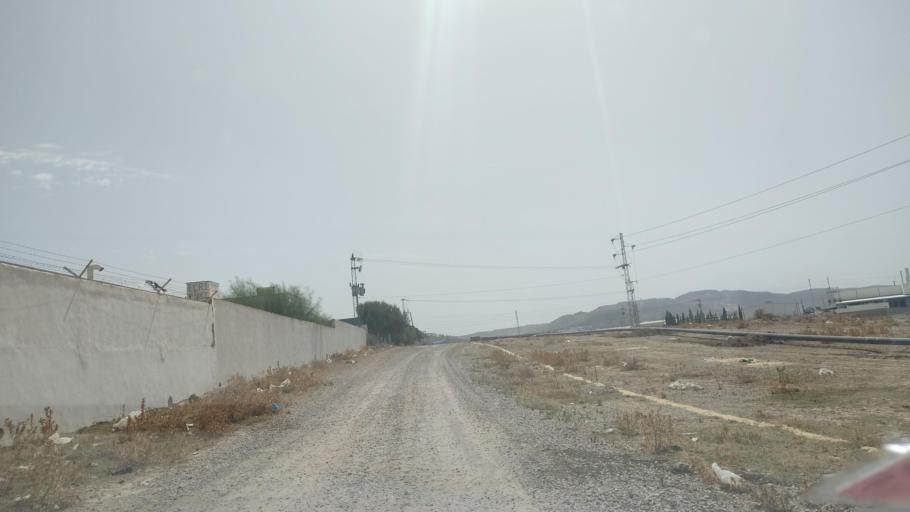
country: TN
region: Tunis
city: La Mohammedia
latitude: 36.5614
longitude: 10.0827
